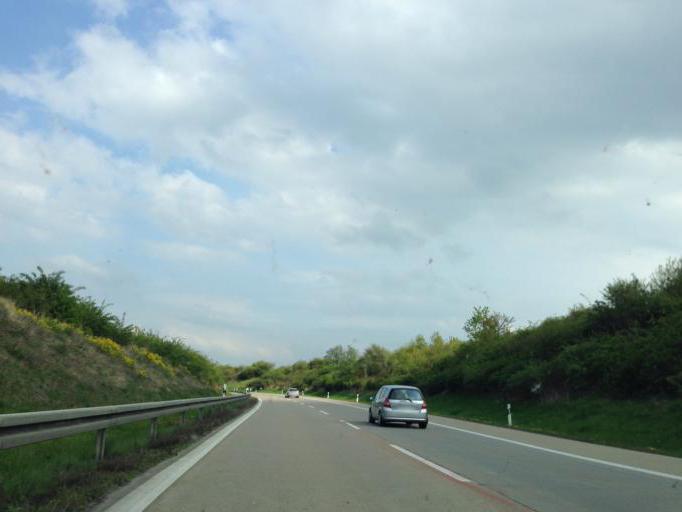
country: DE
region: Saxony
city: Reinsberg
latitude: 51.0538
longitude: 13.3673
